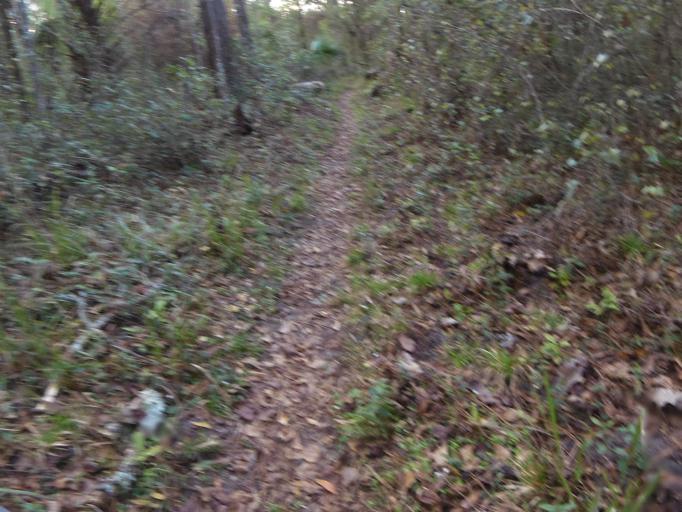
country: US
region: Florida
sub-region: Putnam County
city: Interlachen
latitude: 29.7686
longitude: -81.8333
